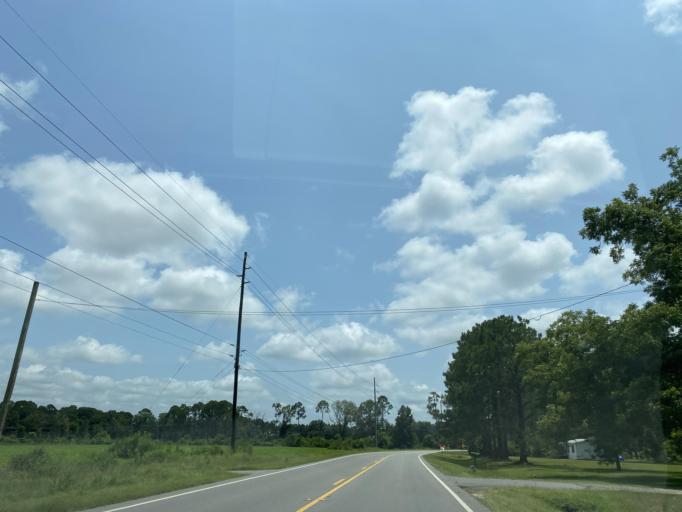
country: US
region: Georgia
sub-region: Jeff Davis County
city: Hazlehurst
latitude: 31.8233
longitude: -82.5695
